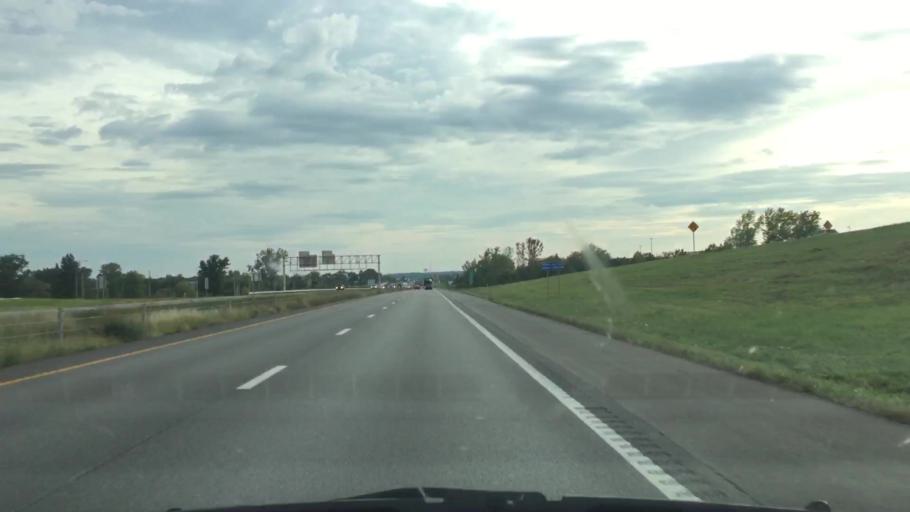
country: US
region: Missouri
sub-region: Clay County
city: Liberty
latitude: 39.2443
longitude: -94.4564
